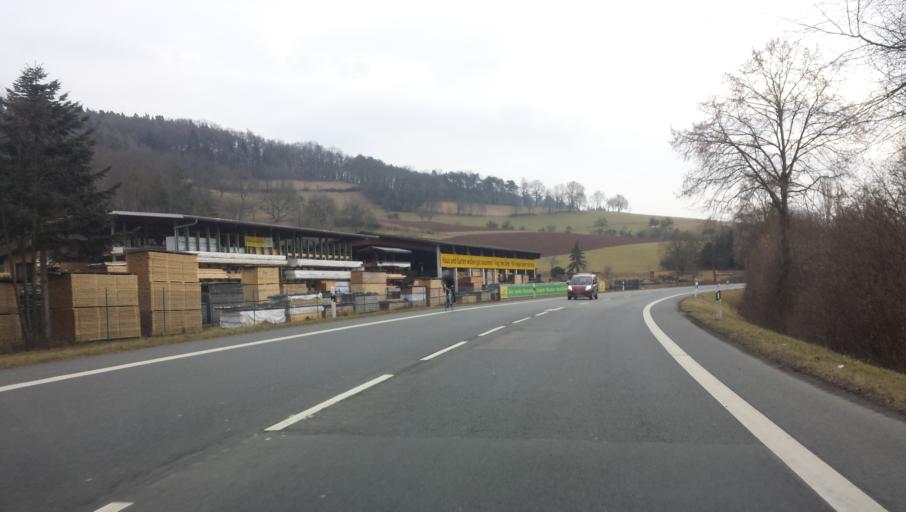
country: DE
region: Hesse
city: Reichelsheim
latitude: 49.7135
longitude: 8.8682
